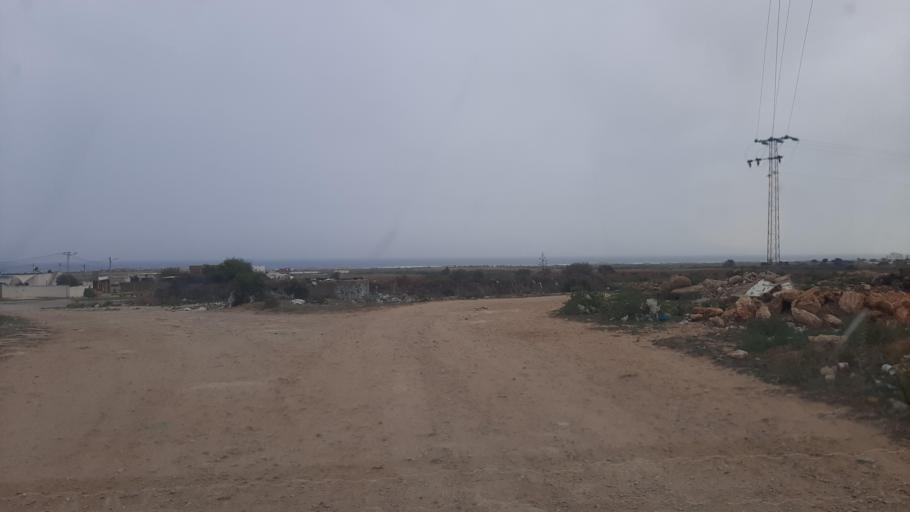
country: TN
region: Nabul
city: Menzel Heurr
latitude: 36.6941
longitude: 10.9356
